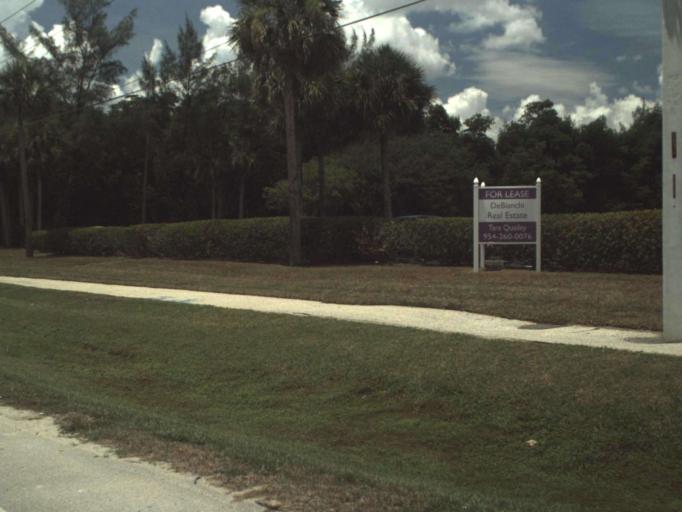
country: US
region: Florida
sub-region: Martin County
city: Jensen Beach
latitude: 27.2570
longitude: -80.1986
